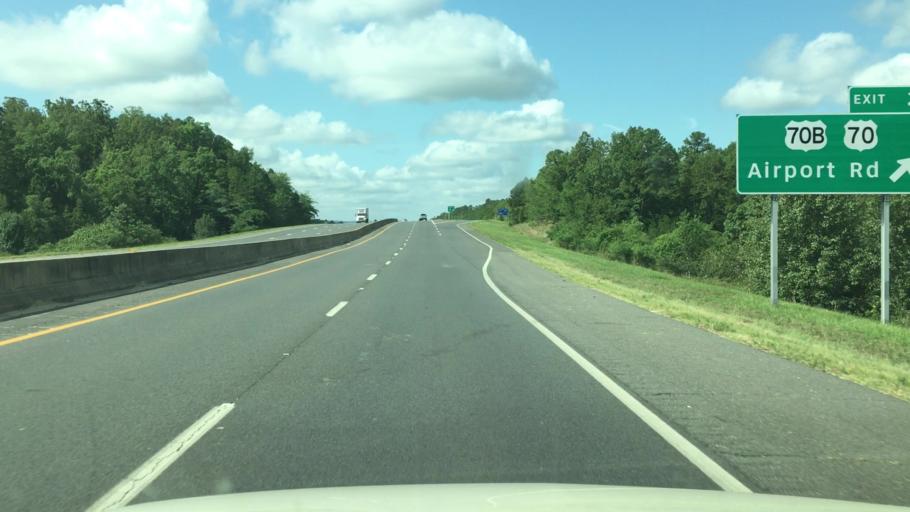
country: US
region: Arkansas
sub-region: Garland County
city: Piney
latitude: 34.4832
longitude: -93.1133
